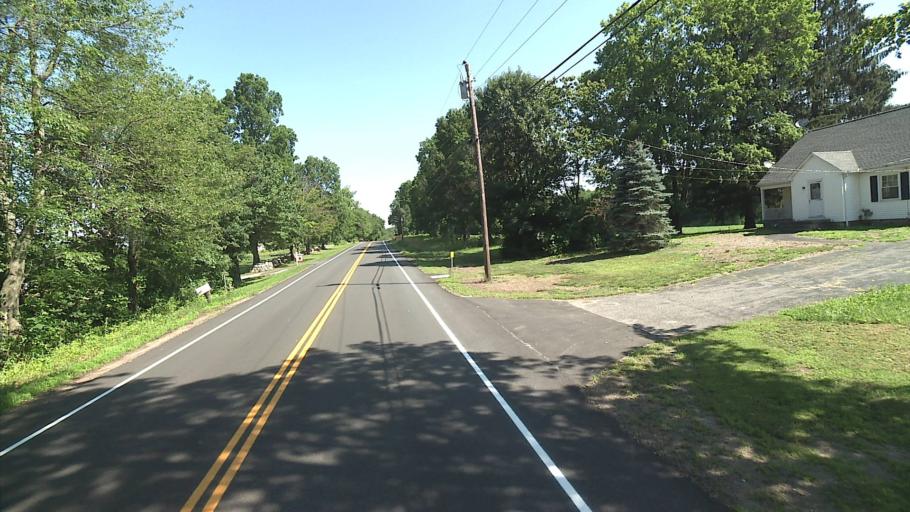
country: US
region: Connecticut
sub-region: Litchfield County
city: Northwest Harwinton
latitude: 41.7582
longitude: -73.0245
